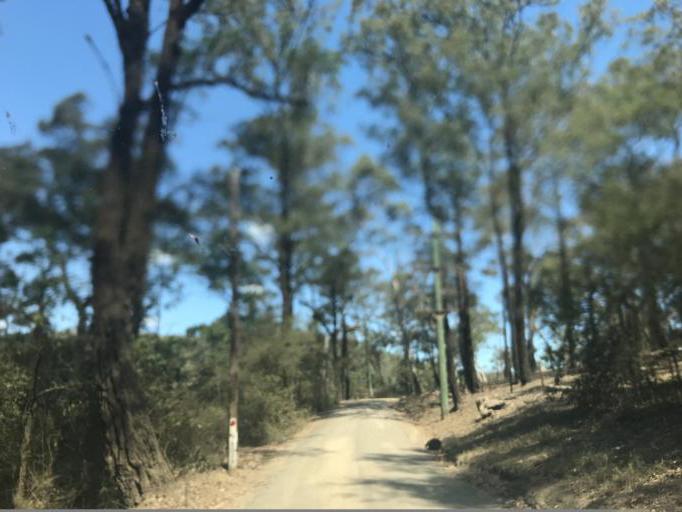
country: AU
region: New South Wales
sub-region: Hawkesbury
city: Pitt Town
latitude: -33.4157
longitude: 150.9160
